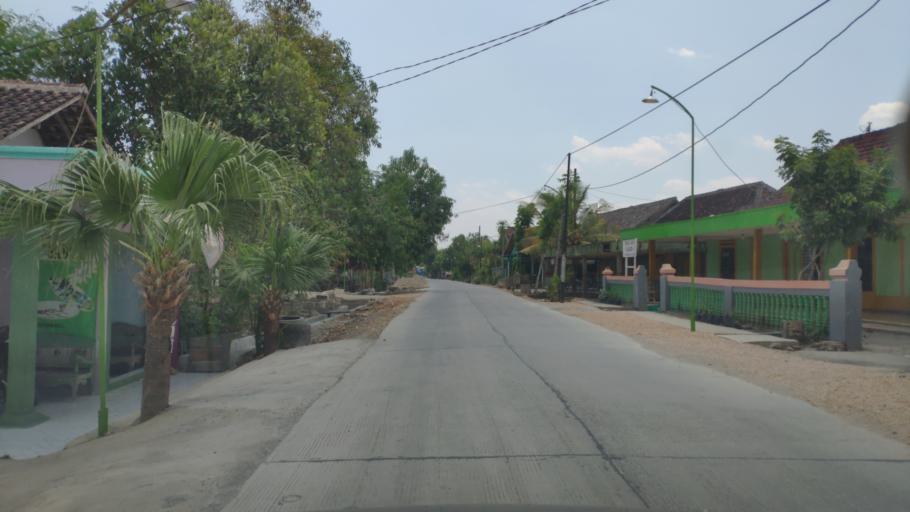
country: ID
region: Central Java
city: Klagen
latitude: -7.2136
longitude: 111.5309
